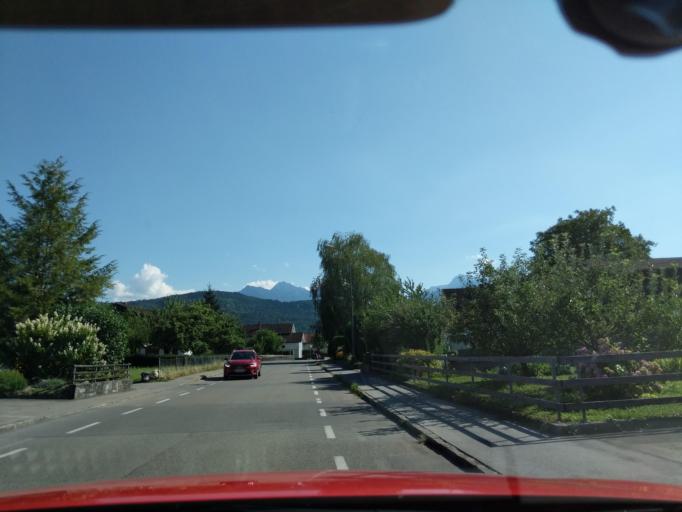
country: AT
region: Vorarlberg
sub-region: Politischer Bezirk Feldkirch
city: Rankweil
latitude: 47.2756
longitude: 9.6307
